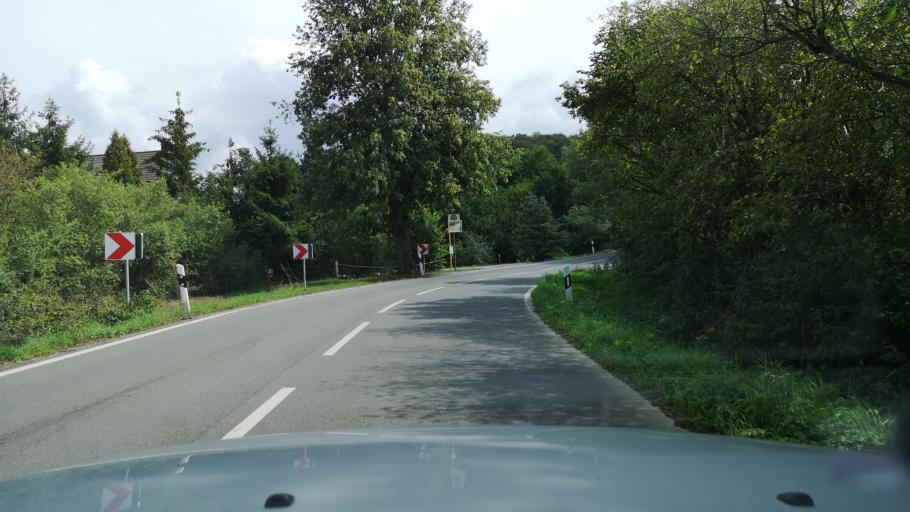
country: DE
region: North Rhine-Westphalia
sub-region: Regierungsbezirk Dusseldorf
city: Wuppertal
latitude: 51.3308
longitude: 7.1439
